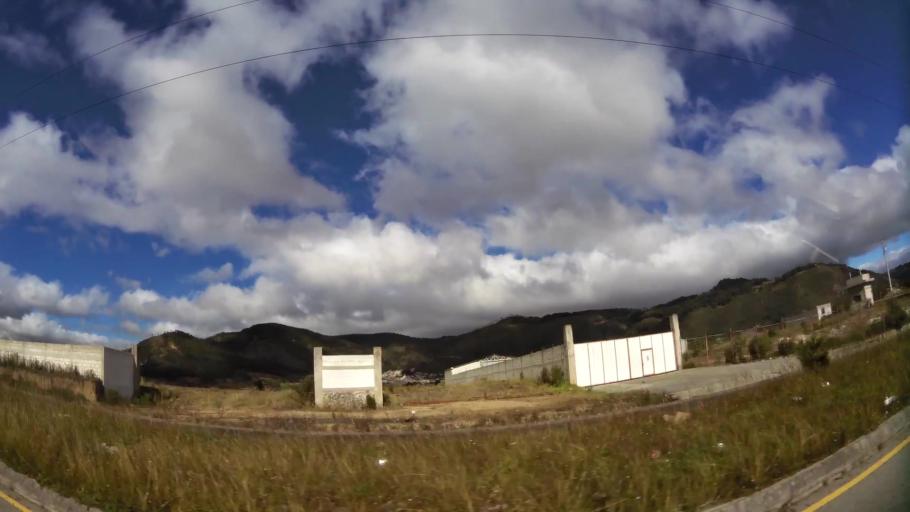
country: GT
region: Quetzaltenango
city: Salcaja
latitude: 14.8933
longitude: -91.4631
